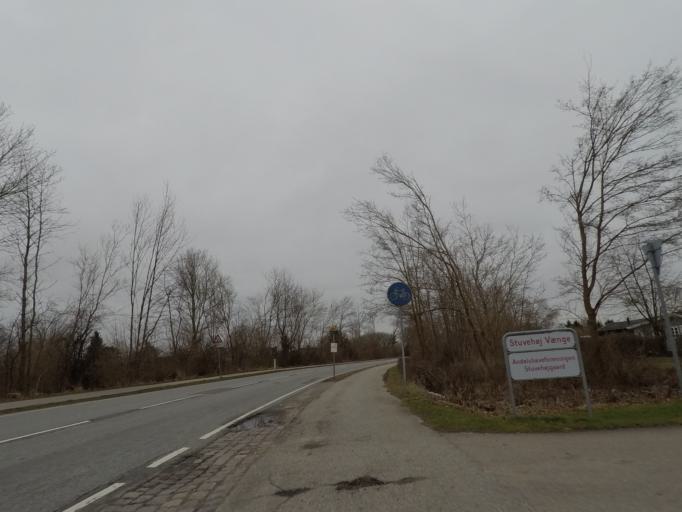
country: DK
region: Capital Region
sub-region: Egedal Kommune
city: Smorumnedre
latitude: 55.7193
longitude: 12.3248
